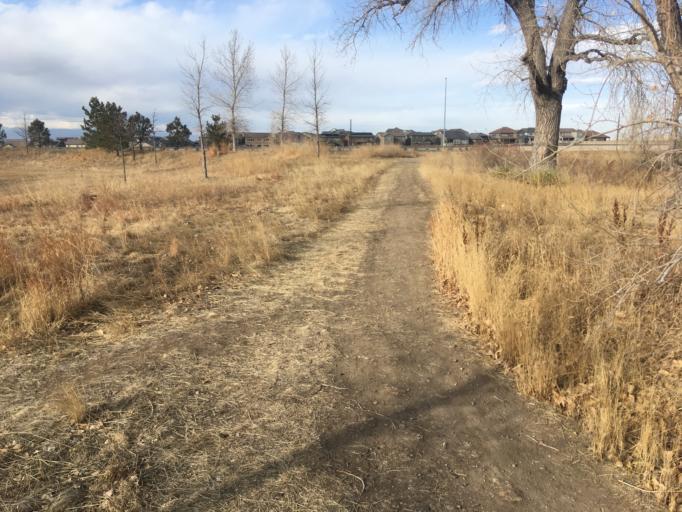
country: US
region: Colorado
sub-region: Boulder County
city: Lafayette
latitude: 39.9824
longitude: -105.0255
